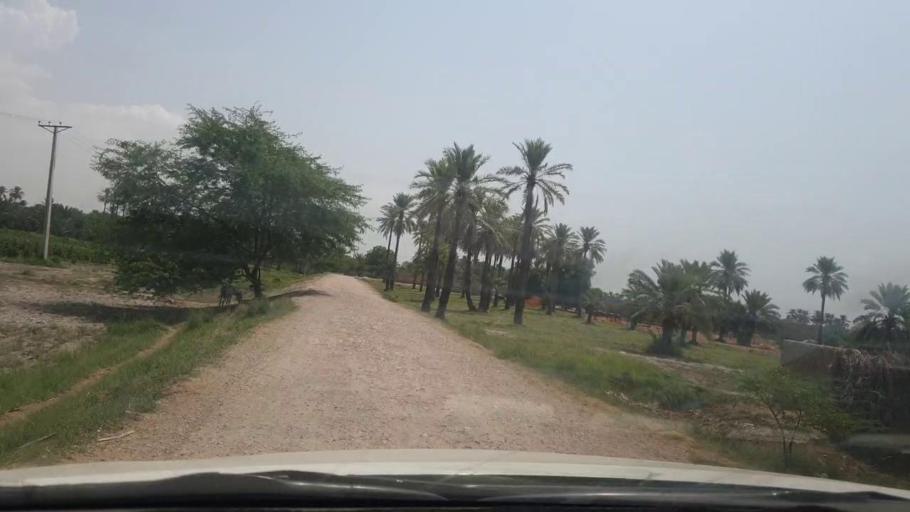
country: PK
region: Sindh
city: Khairpur
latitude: 27.5536
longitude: 68.8277
